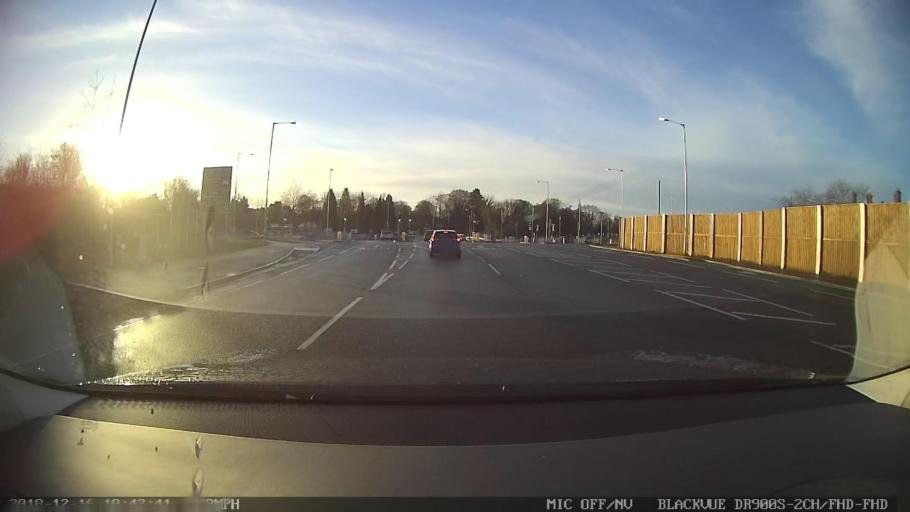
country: GB
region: England
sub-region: Cheshire East
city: Poynton
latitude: 53.3660
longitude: -2.1140
